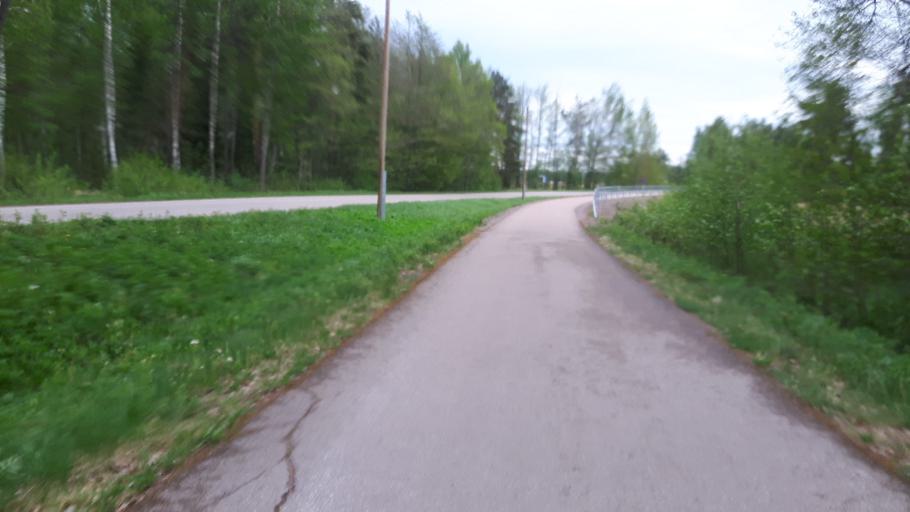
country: FI
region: Kymenlaakso
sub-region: Kotka-Hamina
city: Hamina
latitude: 60.5530
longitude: 27.2290
